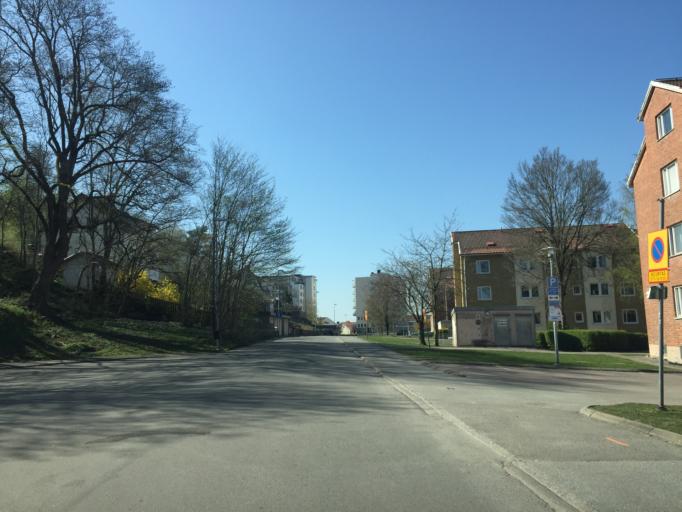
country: SE
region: Vaestra Goetaland
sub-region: Kungalvs Kommun
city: Kungalv
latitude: 57.8746
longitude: 11.9823
